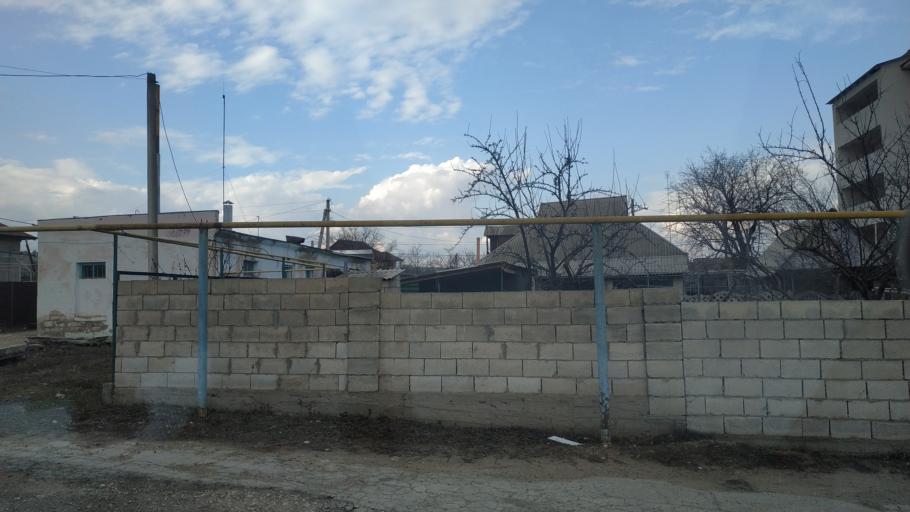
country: MD
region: Anenii Noi
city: Varnita
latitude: 46.8612
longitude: 29.4767
